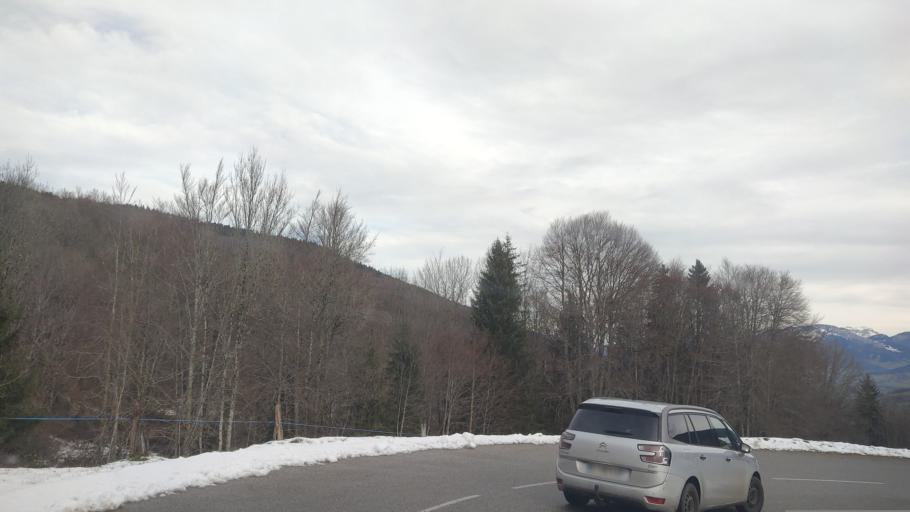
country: FR
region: Rhone-Alpes
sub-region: Departement de la Savoie
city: Mery
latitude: 45.6628
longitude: 6.0353
